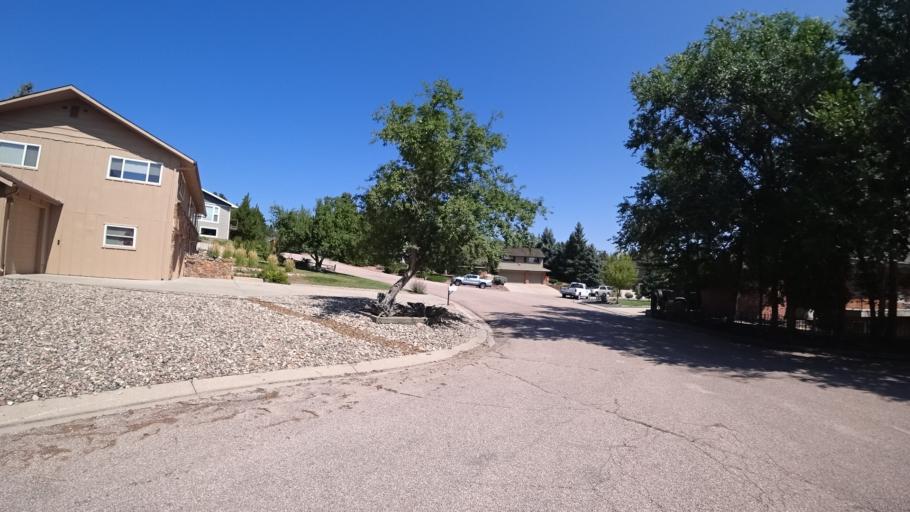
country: US
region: Colorado
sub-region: El Paso County
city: Air Force Academy
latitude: 38.9258
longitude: -104.8234
